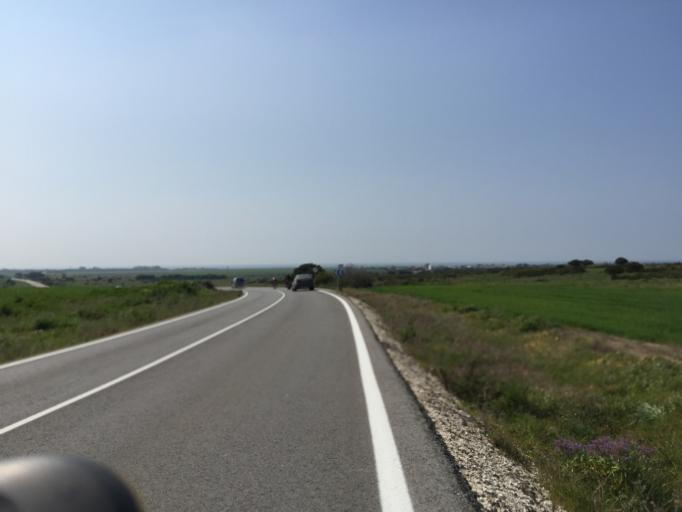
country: ES
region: Andalusia
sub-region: Provincia de Cadiz
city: Conil de la Frontera
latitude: 36.2286
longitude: -6.0388
